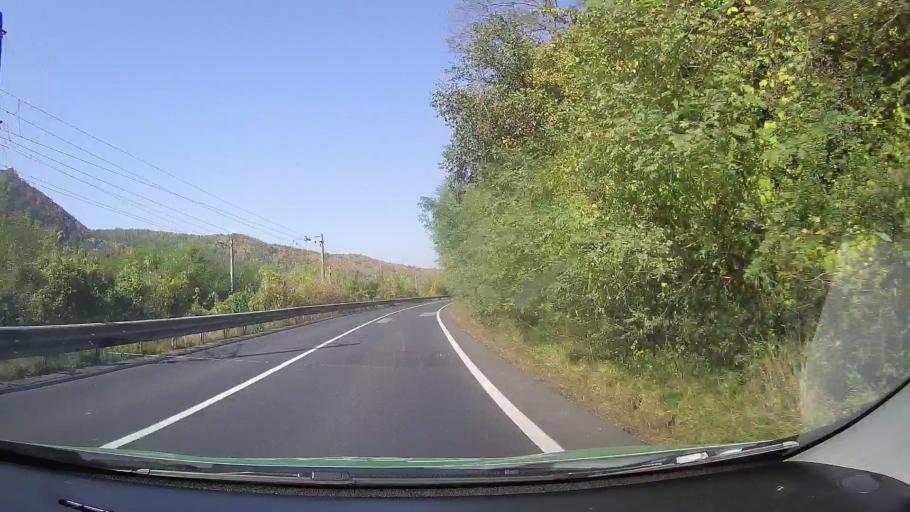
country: RO
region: Hunedoara
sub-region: Comuna Zam
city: Zam
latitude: 45.9756
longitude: 22.4334
